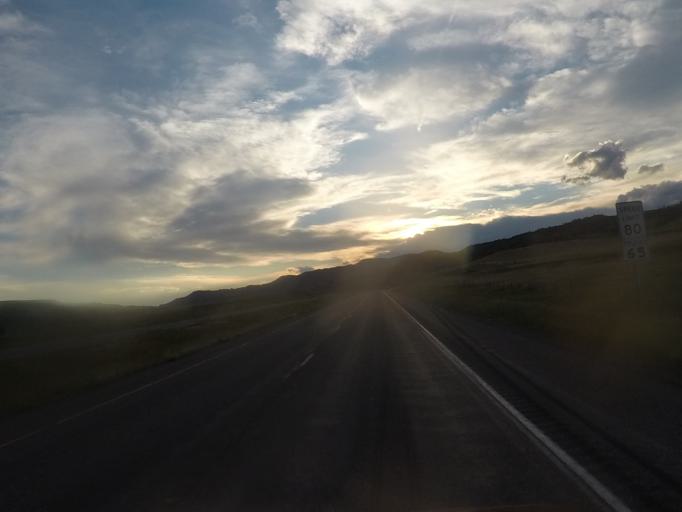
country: US
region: Montana
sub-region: Park County
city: Livingston
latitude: 45.6552
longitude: -110.6237
